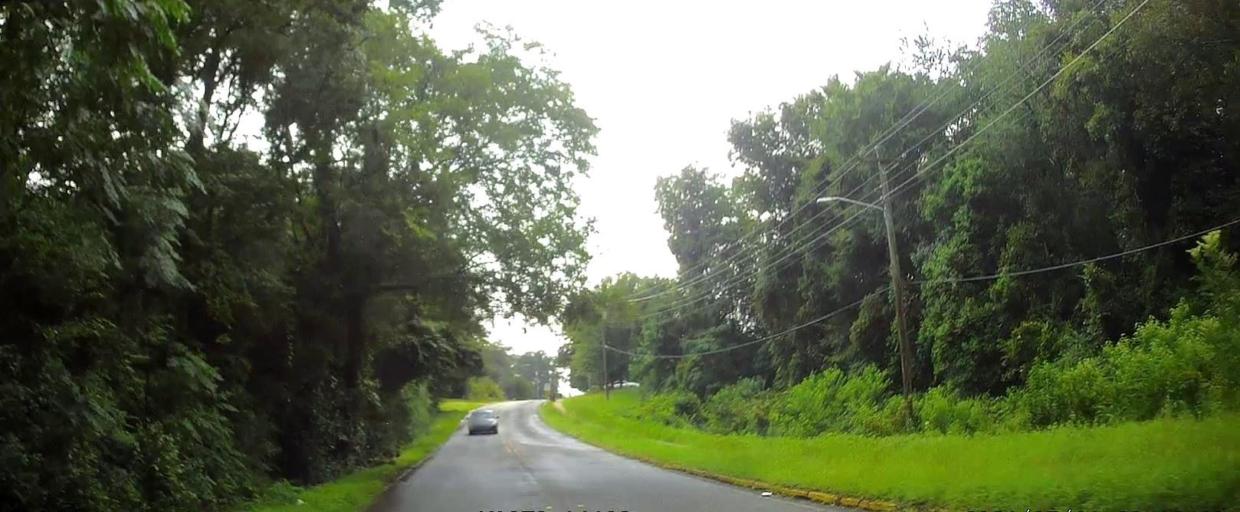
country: US
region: Georgia
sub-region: Houston County
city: Warner Robins
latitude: 32.6482
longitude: -83.6138
